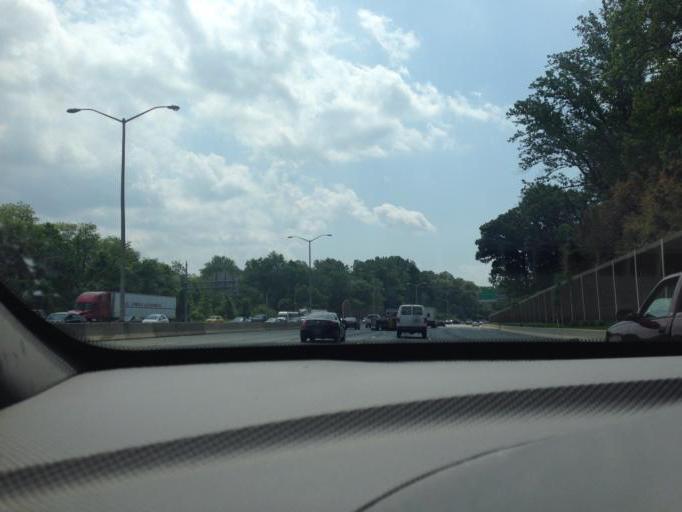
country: US
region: Maryland
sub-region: Baltimore County
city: Pikesville
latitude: 39.3969
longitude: -76.6862
